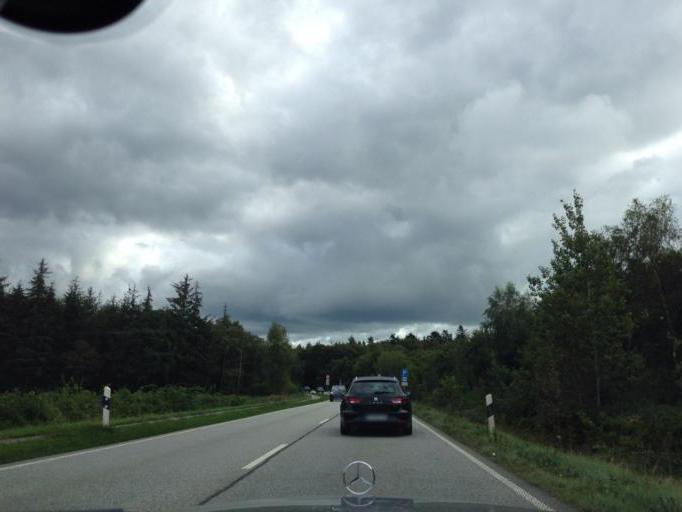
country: DE
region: Schleswig-Holstein
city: Leck
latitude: 54.7609
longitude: 8.9840
